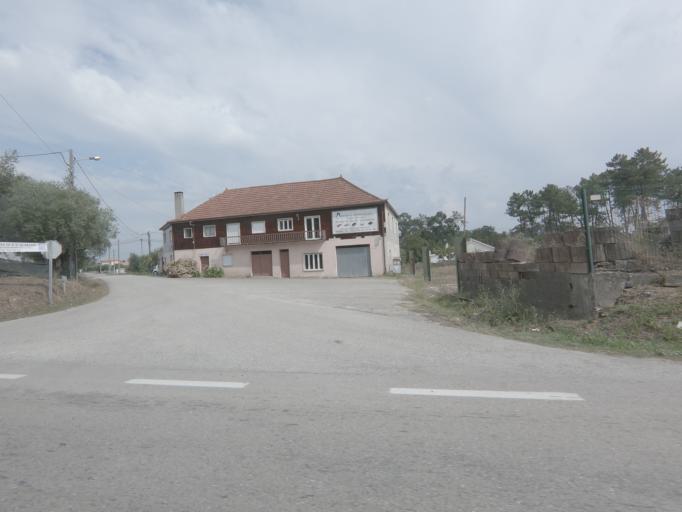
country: PT
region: Leiria
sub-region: Pombal
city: Pombal
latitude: 39.8622
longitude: -8.6983
